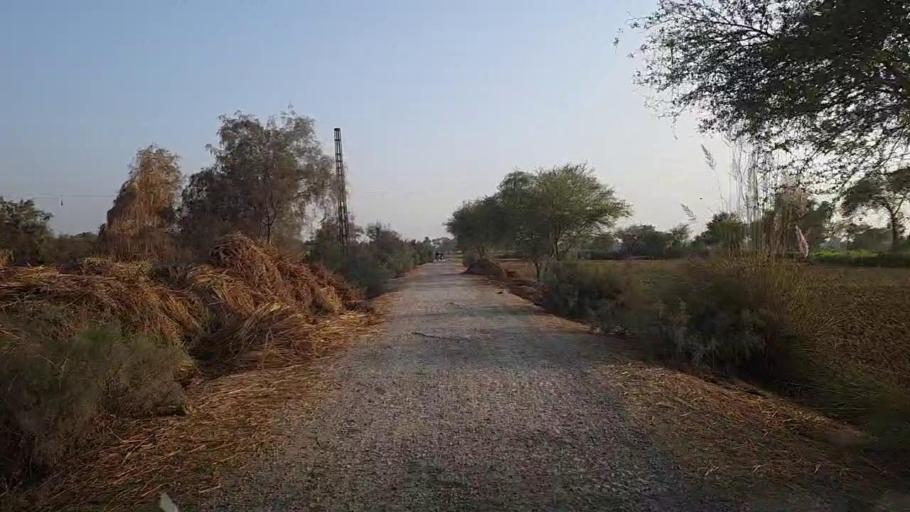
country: PK
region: Sindh
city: Kandhkot
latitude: 28.2367
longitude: 69.0910
